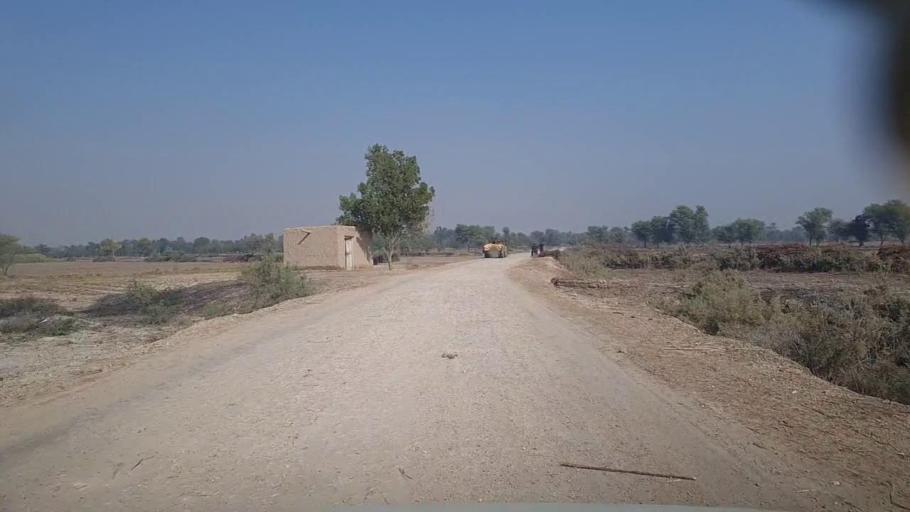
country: PK
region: Sindh
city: Kandiari
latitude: 26.9334
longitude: 68.5264
